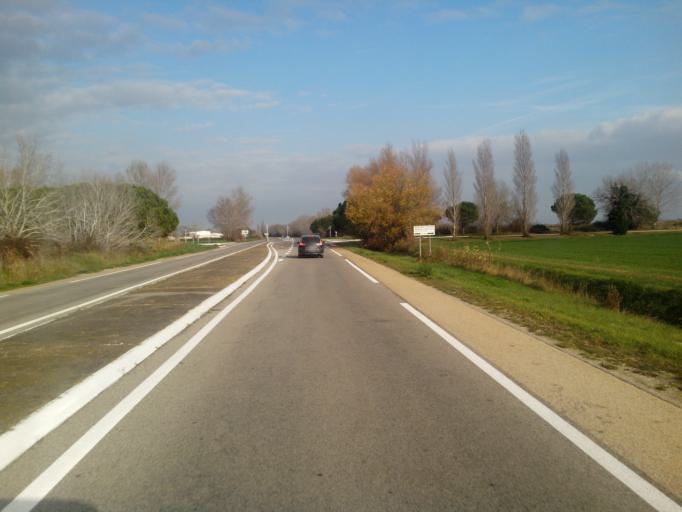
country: FR
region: Languedoc-Roussillon
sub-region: Departement du Gard
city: Saint-Gilles
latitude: 43.5902
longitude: 4.4646
